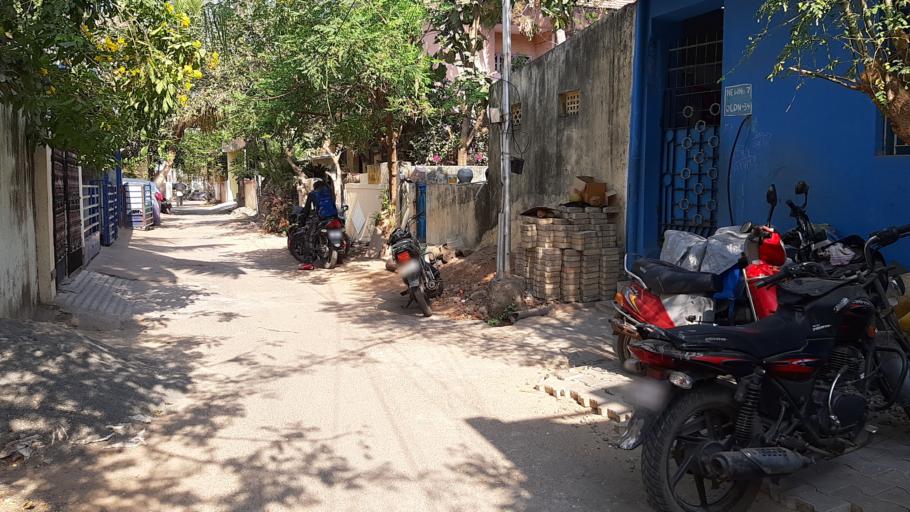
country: IN
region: Tamil Nadu
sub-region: Kancheepuram
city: Alandur
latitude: 12.9865
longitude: 80.2275
